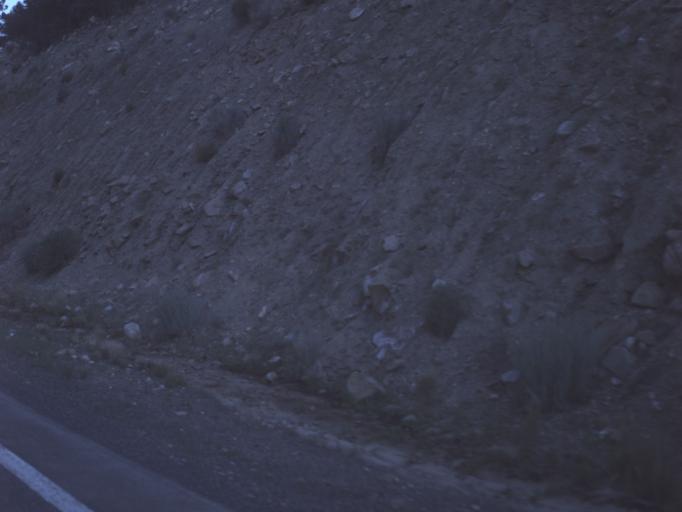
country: US
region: Utah
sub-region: Emery County
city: Huntington
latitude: 39.4167
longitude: -111.1224
